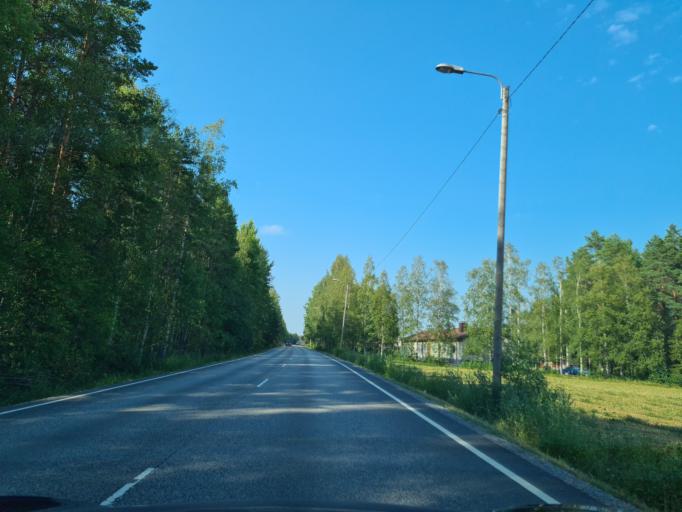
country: FI
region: Satakunta
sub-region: Pohjois-Satakunta
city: Kankaanpaeae
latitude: 61.9476
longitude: 22.5129
